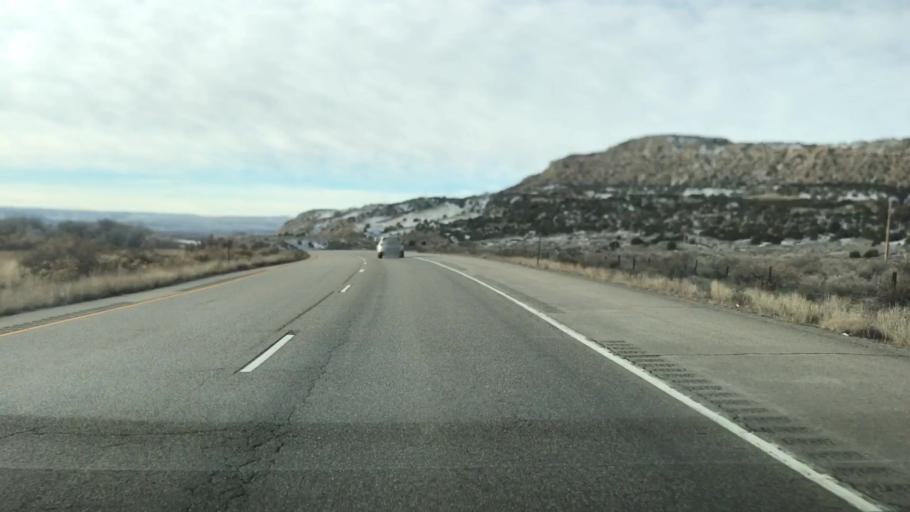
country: US
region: Colorado
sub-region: Garfield County
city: Parachute
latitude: 39.3463
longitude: -108.1891
